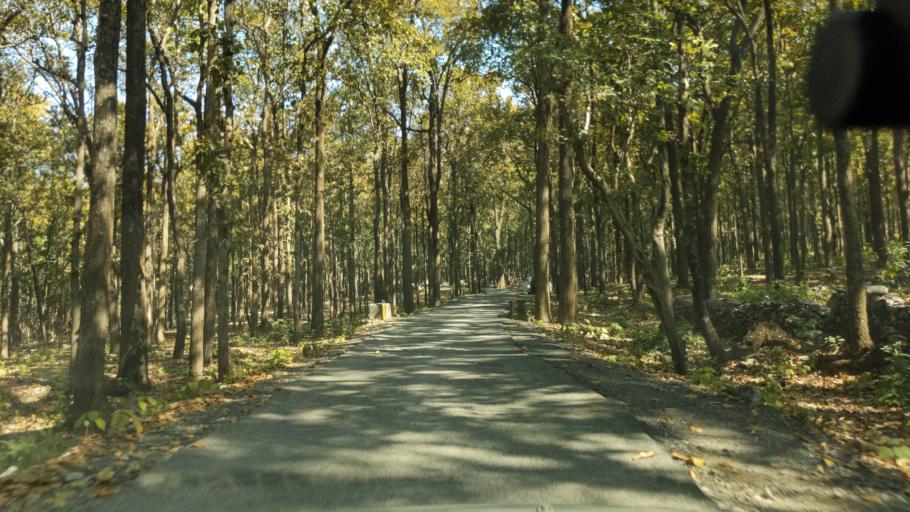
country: IN
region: Uttarakhand
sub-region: Naini Tal
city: Ramnagar
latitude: 29.4677
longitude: 79.2329
